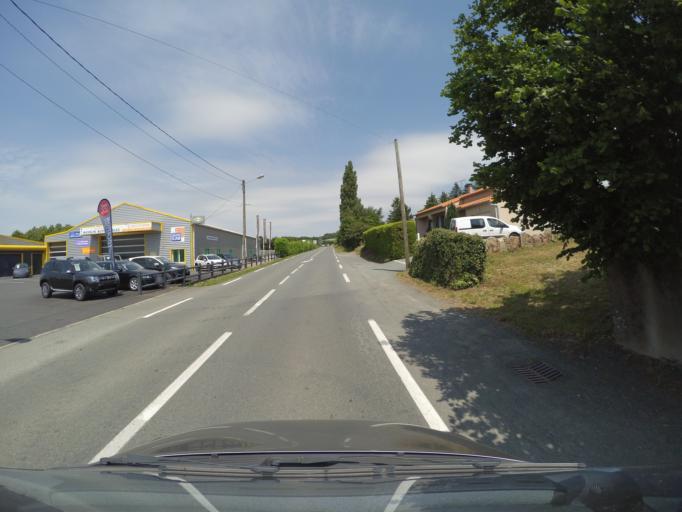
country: FR
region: Pays de la Loire
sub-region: Departement de la Vendee
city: Saint-Michel-Mont-Mercure
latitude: 46.8363
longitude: -0.9058
